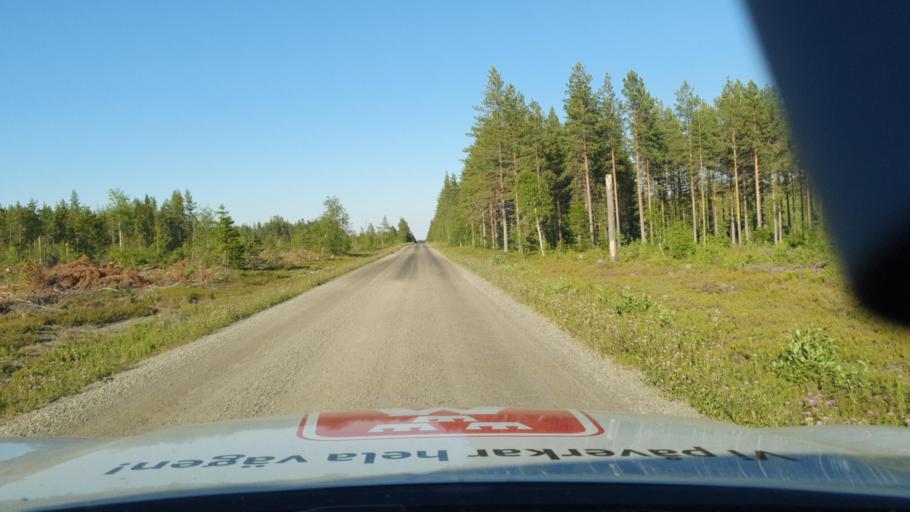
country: SE
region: Vaesterbotten
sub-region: Skelleftea Kommun
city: Burea
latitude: 64.5067
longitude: 21.3089
